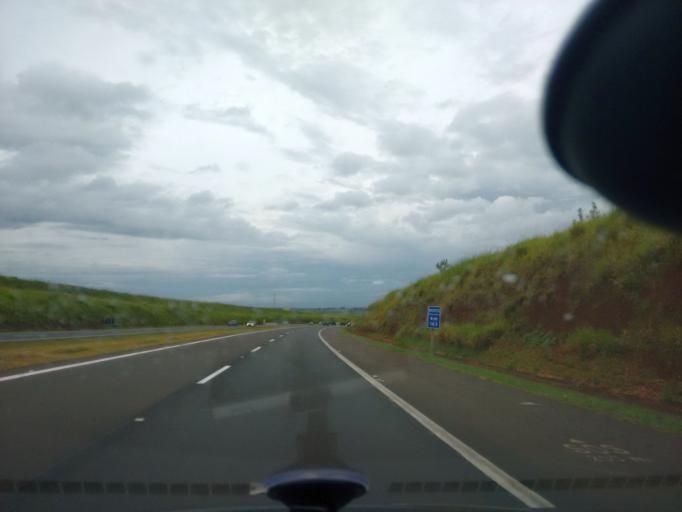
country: BR
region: Sao Paulo
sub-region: Cordeiropolis
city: Cordeiropolis
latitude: -22.5309
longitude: -47.4459
